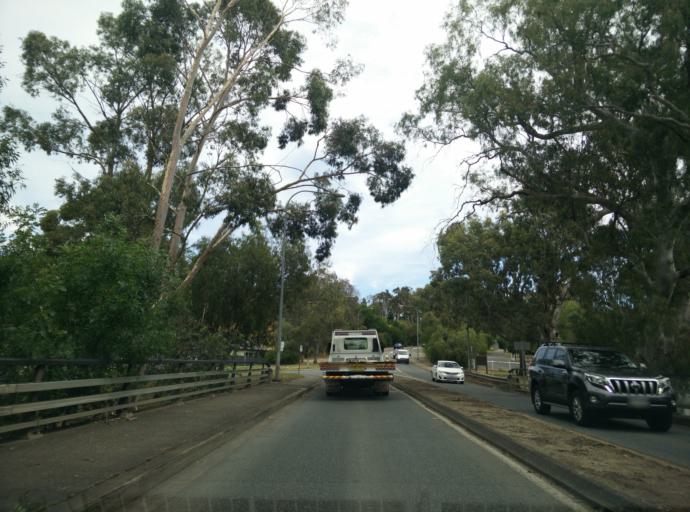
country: AU
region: South Australia
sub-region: Mitcham
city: Mitcham
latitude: -34.9807
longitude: 138.6223
